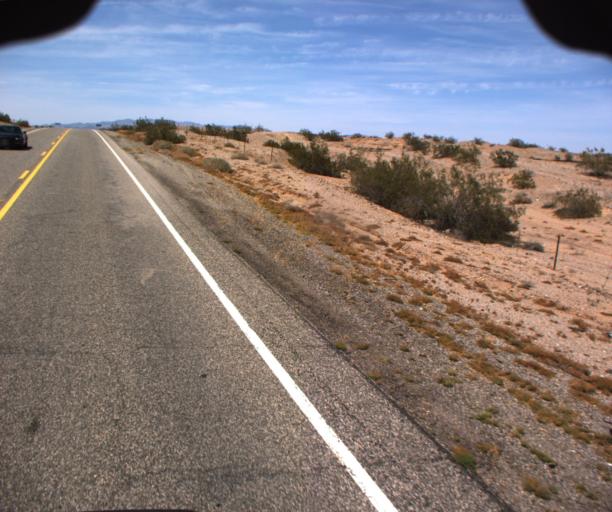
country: US
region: Arizona
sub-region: La Paz County
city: Parker
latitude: 34.0209
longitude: -114.2504
